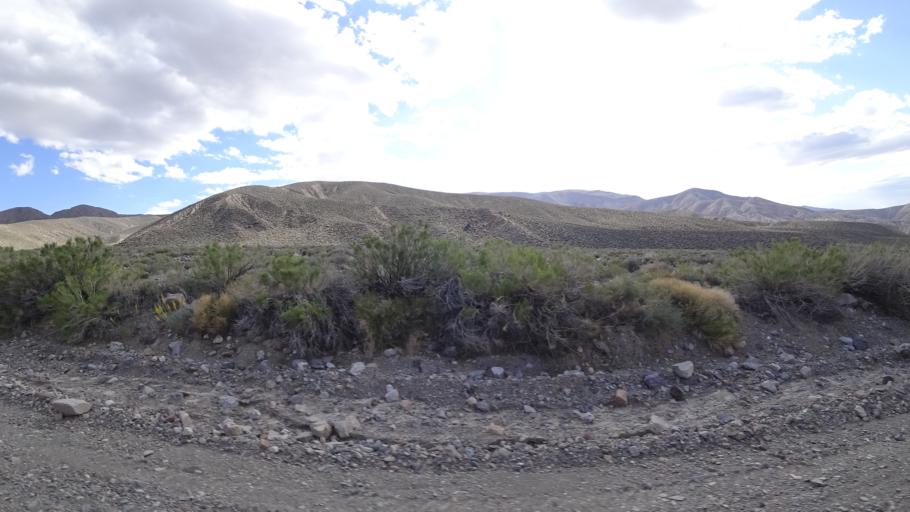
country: US
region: Nevada
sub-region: Nye County
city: Beatty
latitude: 36.4077
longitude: -117.1718
